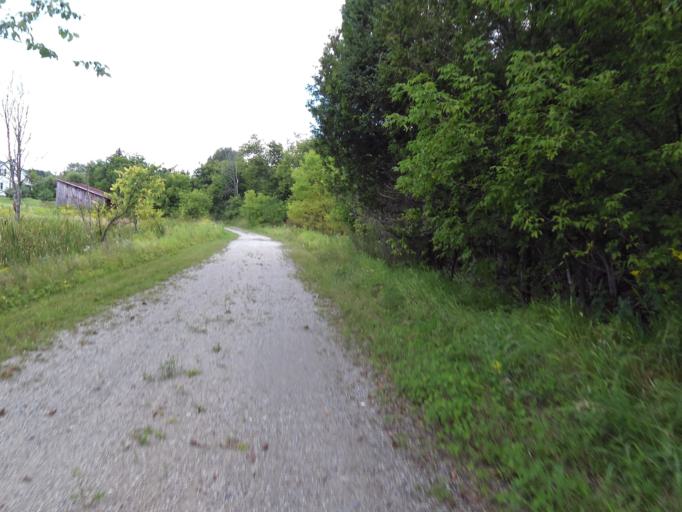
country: CA
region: Quebec
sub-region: Outaouais
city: Wakefield
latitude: 45.8476
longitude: -75.9863
